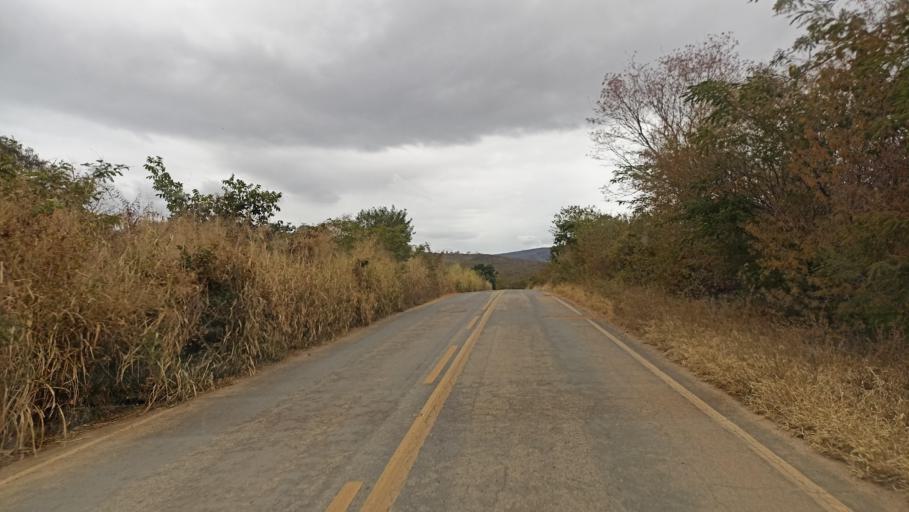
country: BR
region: Minas Gerais
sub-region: Itinga
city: Itinga
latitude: -16.6536
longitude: -41.8311
